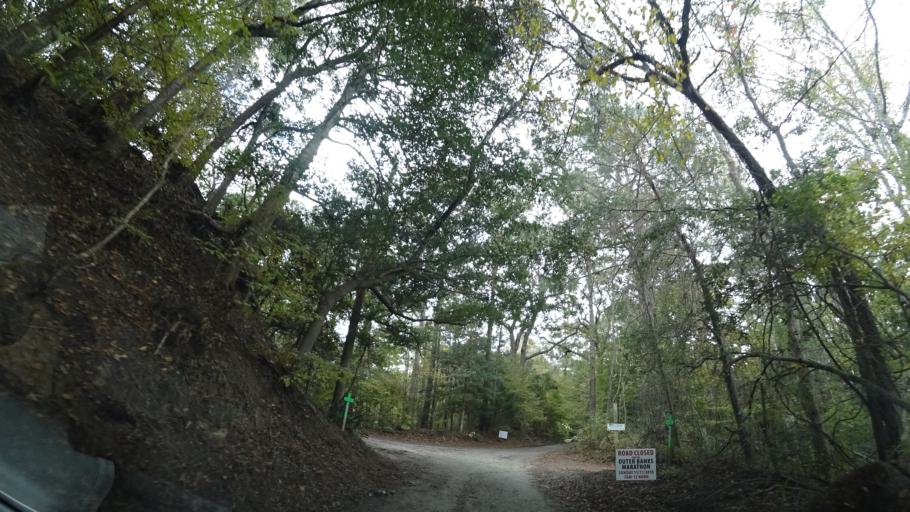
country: US
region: North Carolina
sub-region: Dare County
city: Kill Devil Hills
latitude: 35.9899
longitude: -75.6669
